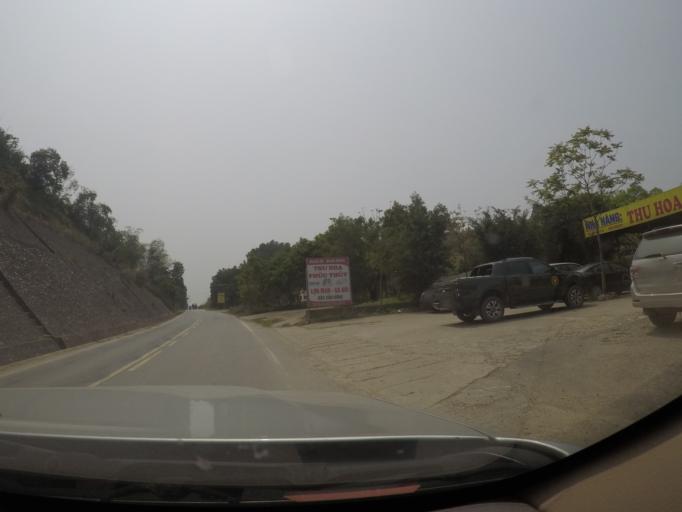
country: VN
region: Thanh Hoa
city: Thi Tran Yen Cat
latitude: 19.6674
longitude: 105.4300
